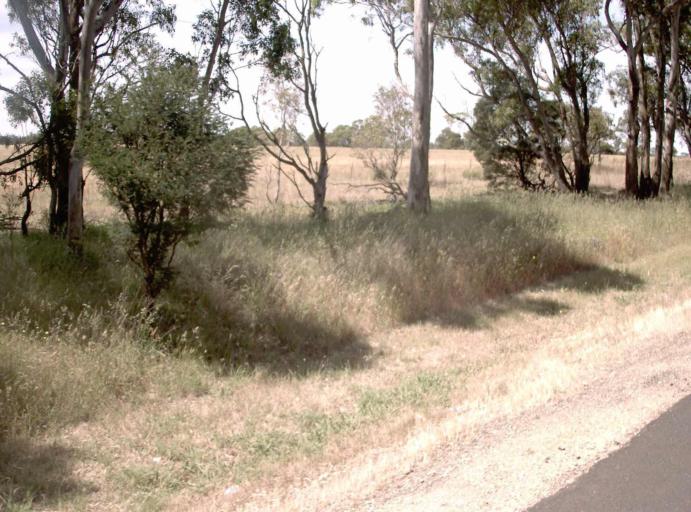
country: AU
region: Victoria
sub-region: Wellington
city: Sale
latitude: -37.9316
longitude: 147.1912
